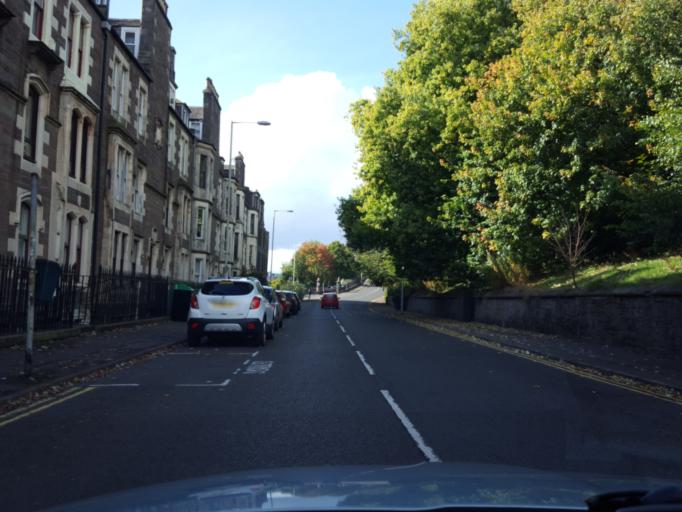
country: GB
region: Scotland
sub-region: Dundee City
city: Dundee
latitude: 56.4645
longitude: -2.9771
